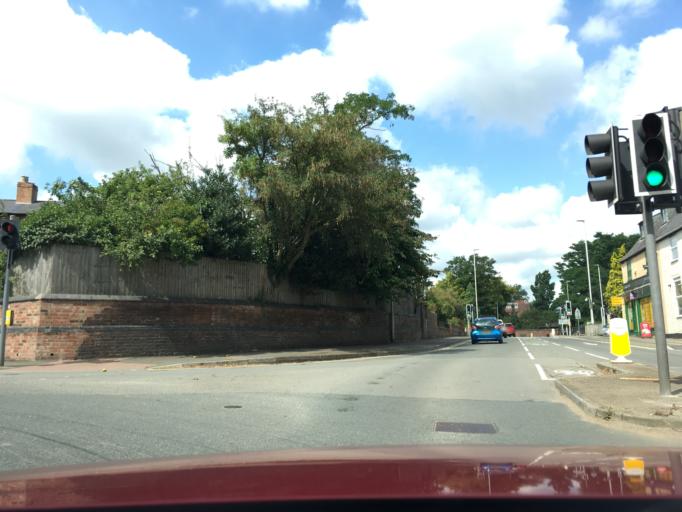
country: GB
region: England
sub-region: Gloucestershire
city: Gloucester
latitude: 51.8686
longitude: -2.2262
